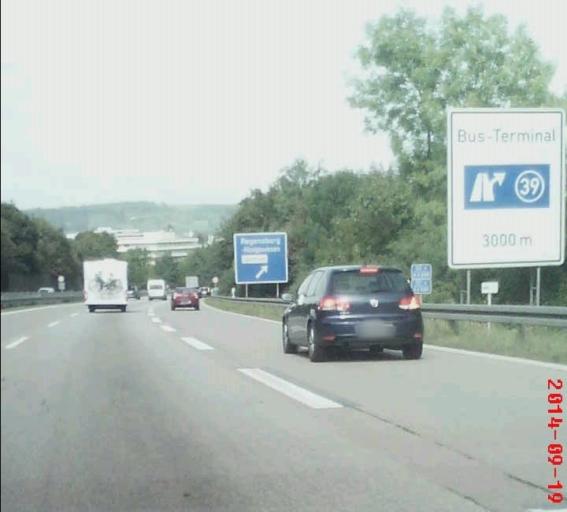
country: DE
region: Bavaria
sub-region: Upper Palatinate
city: Pentling
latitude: 49.0041
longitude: 12.0618
